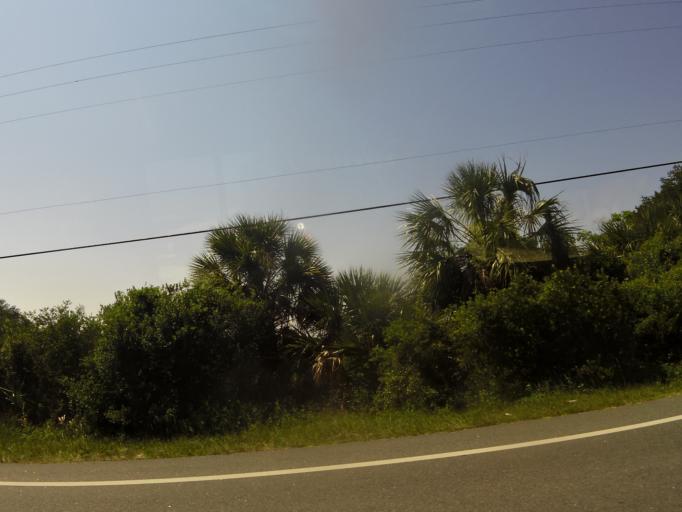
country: US
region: Florida
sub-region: Duval County
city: Atlantic Beach
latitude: 30.3894
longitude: -81.4422
